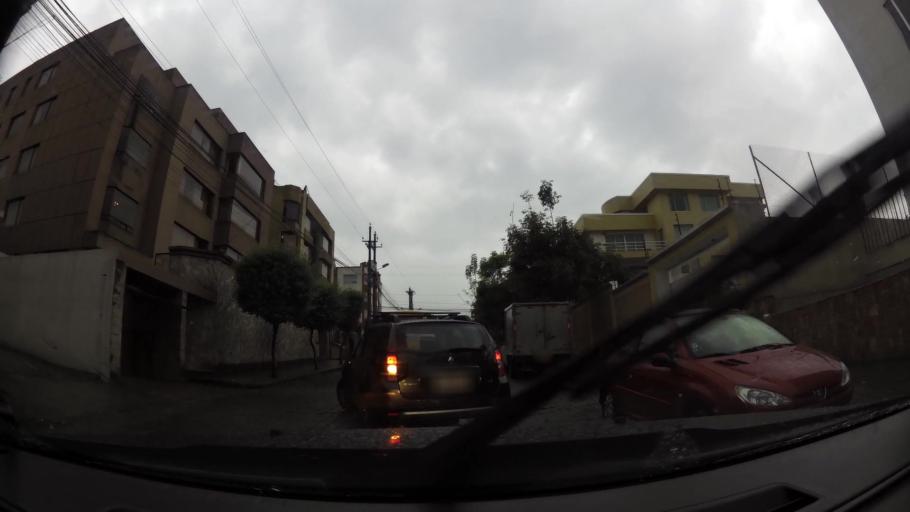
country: EC
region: Pichincha
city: Quito
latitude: -0.1561
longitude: -78.4626
